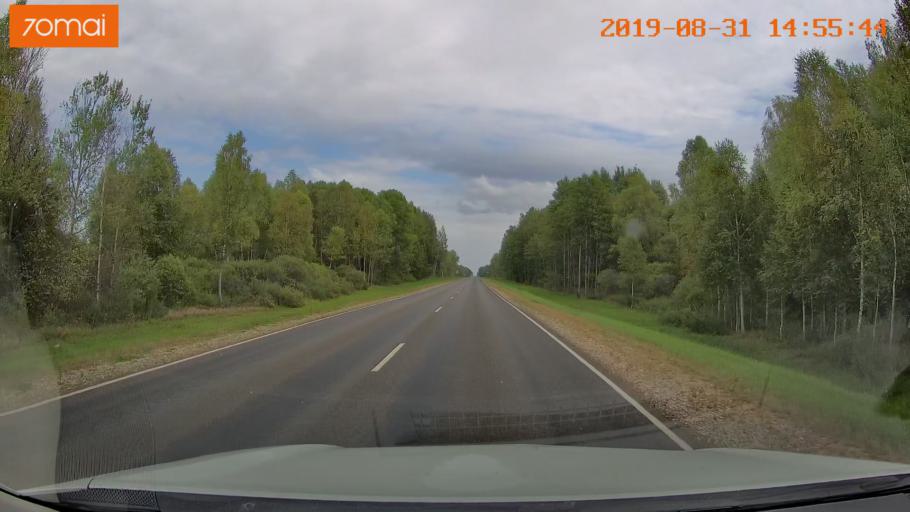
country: RU
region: Kaluga
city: Spas-Demensk
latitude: 54.3000
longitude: 33.9214
